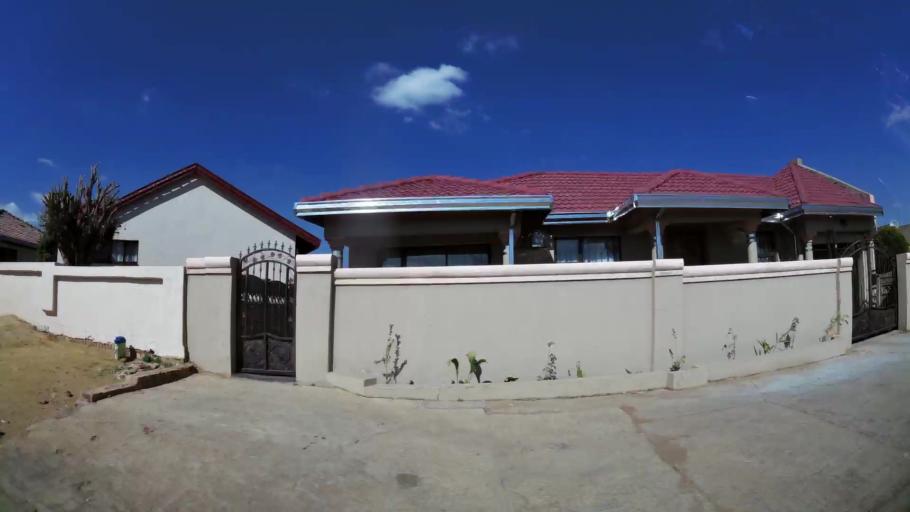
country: ZA
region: Gauteng
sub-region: West Rand District Municipality
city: Krugersdorp
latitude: -26.1540
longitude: 27.7708
